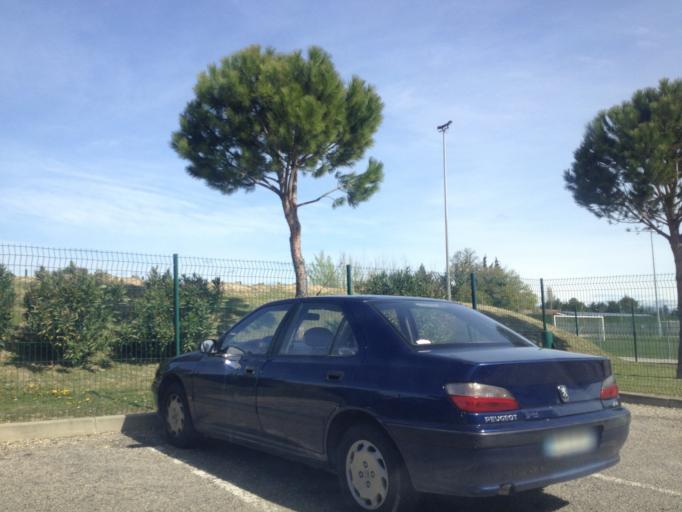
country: FR
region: Provence-Alpes-Cote d'Azur
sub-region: Departement du Vaucluse
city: Camaret-sur-Aigues
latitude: 44.1651
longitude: 4.8789
